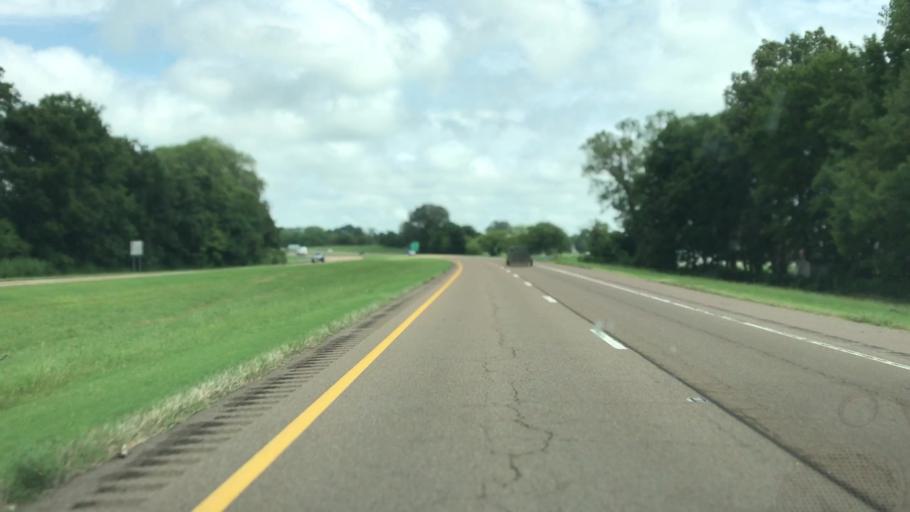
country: US
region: Tennessee
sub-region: Dyer County
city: Dyersburg
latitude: 36.0675
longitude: -89.3622
